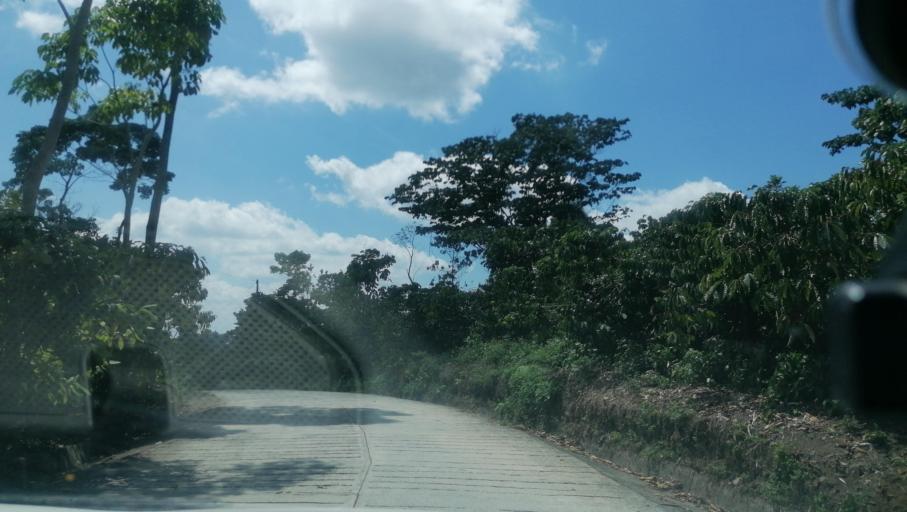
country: MX
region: Chiapas
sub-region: Cacahoatan
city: Benito Juarez
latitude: 15.0579
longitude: -92.1470
